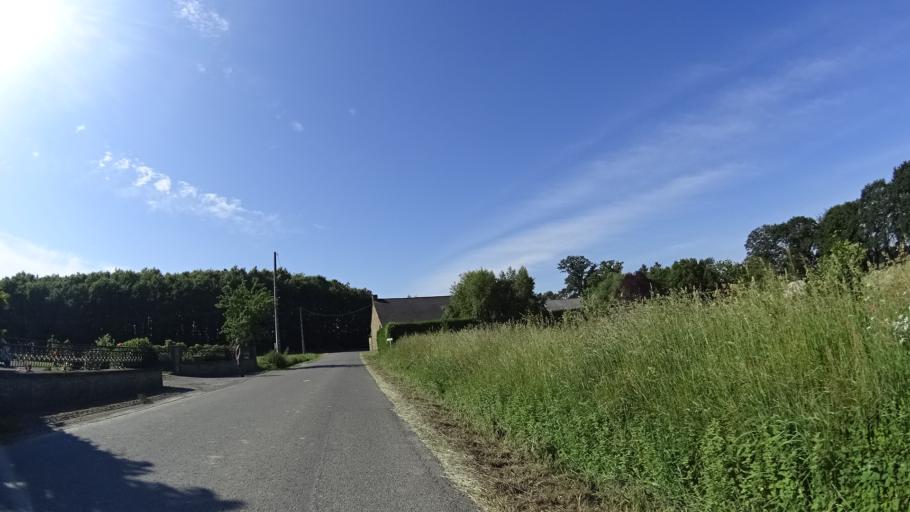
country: FR
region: Brittany
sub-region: Departement d'Ille-et-Vilaine
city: Guipry
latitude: 47.8024
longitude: -1.8489
